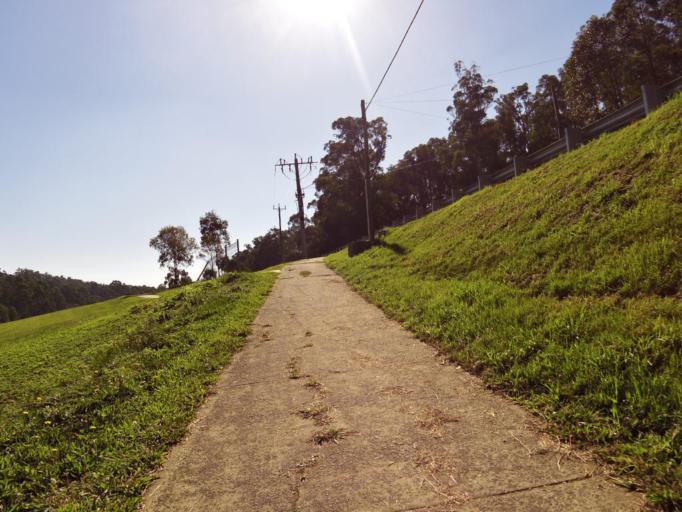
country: AU
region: Victoria
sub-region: Cardinia
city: Cockatoo
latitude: -37.9405
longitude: 145.4927
